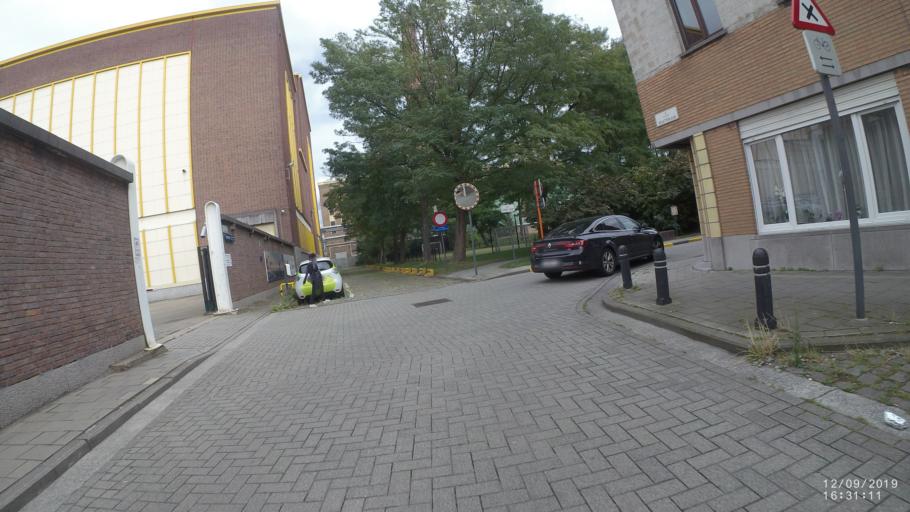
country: BE
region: Flanders
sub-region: Provincie Oost-Vlaanderen
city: Gent
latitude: 51.0595
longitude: 3.7341
